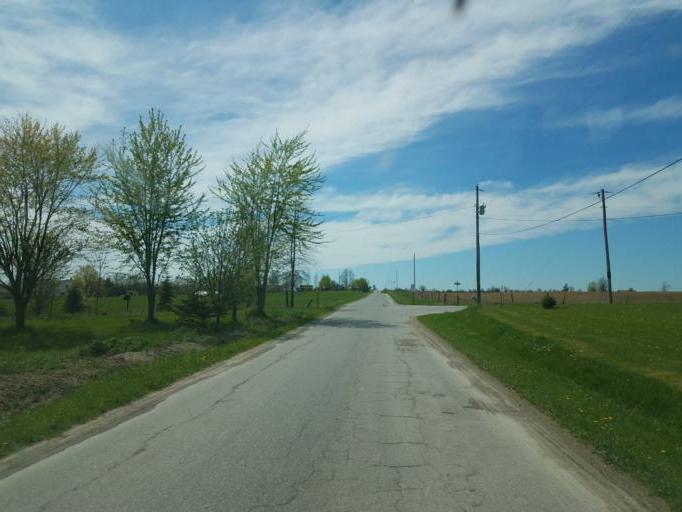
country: US
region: Ohio
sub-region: Ashland County
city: Ashland
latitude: 40.9166
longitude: -82.4063
